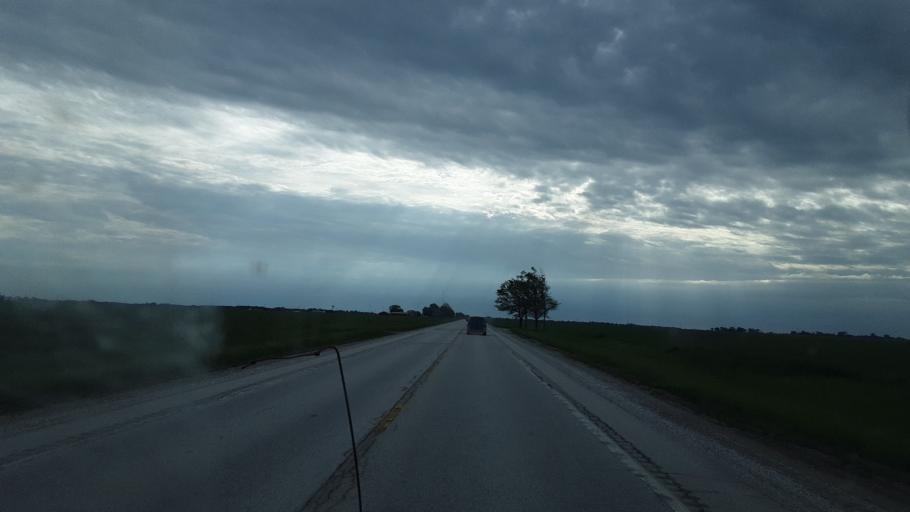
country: US
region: Illinois
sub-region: Hancock County
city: Carthage
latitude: 40.4027
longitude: -91.1940
